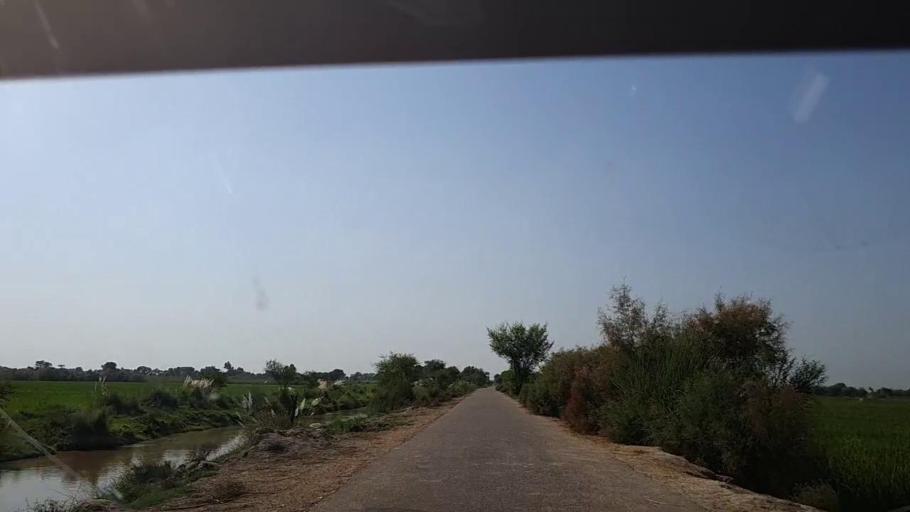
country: PK
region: Sindh
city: Ghauspur
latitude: 28.2048
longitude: 69.0345
